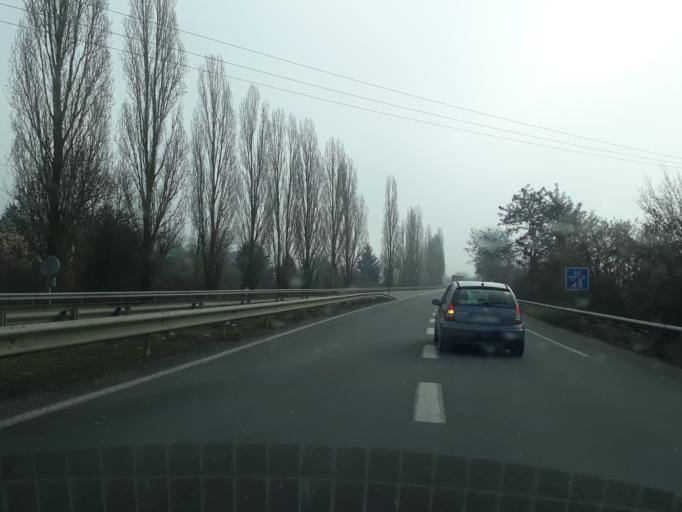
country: FR
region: Lorraine
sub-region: Departement de Meurthe-et-Moselle
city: Bouxieres-aux-Dames
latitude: 48.7500
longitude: 6.1601
